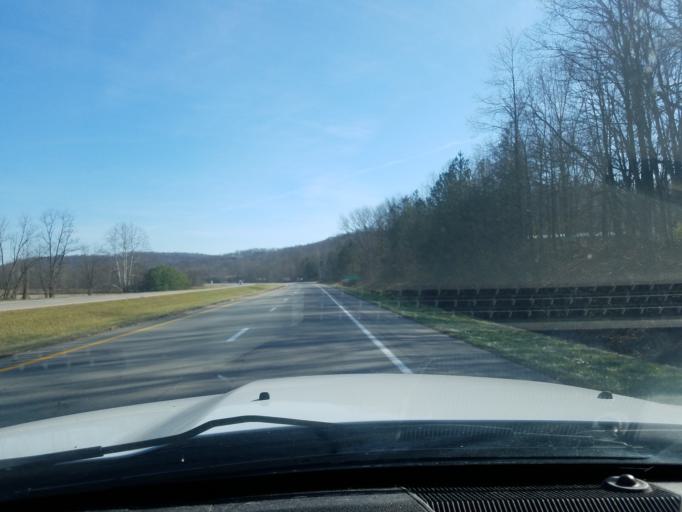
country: US
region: Ohio
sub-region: Pike County
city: Piketon
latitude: 39.0432
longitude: -83.1683
